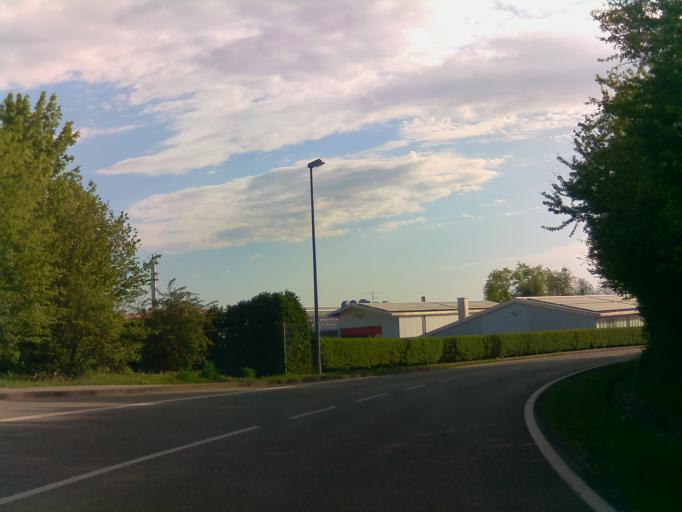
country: DE
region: Baden-Wuerttemberg
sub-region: Tuebingen Region
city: Rosenfeld
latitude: 48.2848
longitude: 8.7162
